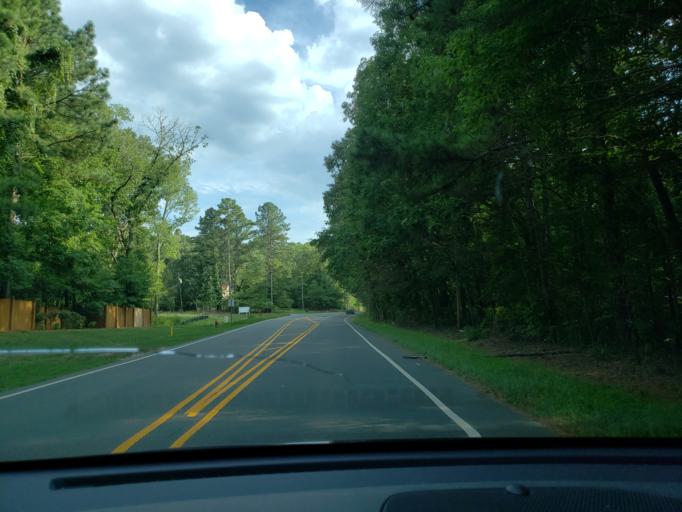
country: US
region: North Carolina
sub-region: Orange County
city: Chapel Hill
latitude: 35.8934
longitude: -78.9807
